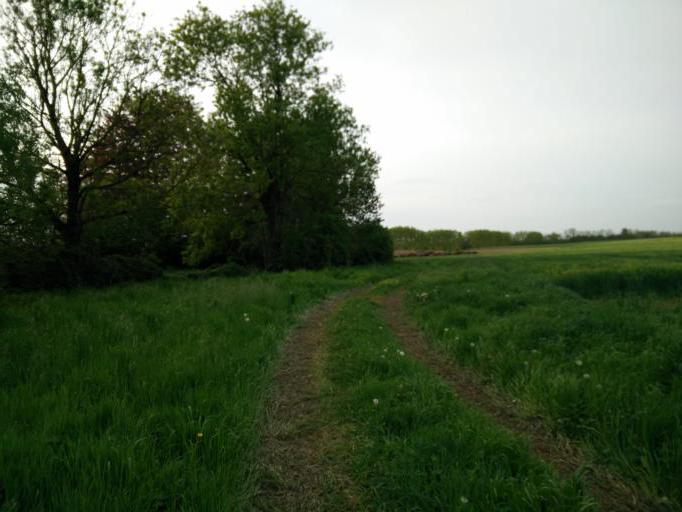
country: BE
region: Wallonia
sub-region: Province de Liege
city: Dalhem
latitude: 50.7375
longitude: 5.7560
